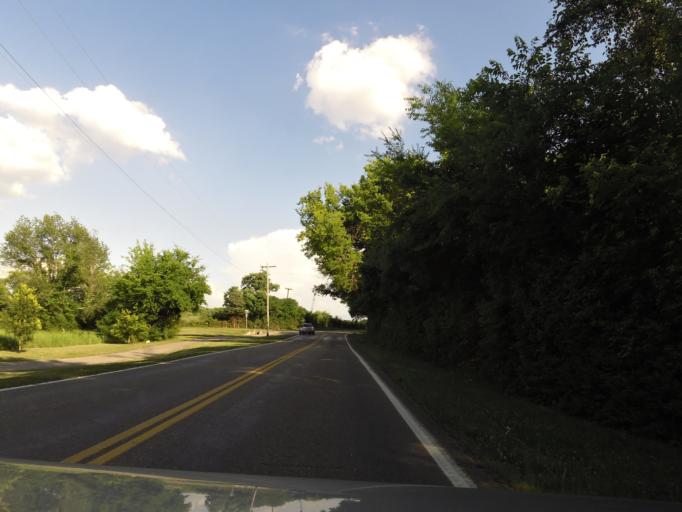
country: US
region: Tennessee
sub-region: Blount County
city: Alcoa
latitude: 35.7850
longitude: -83.9693
